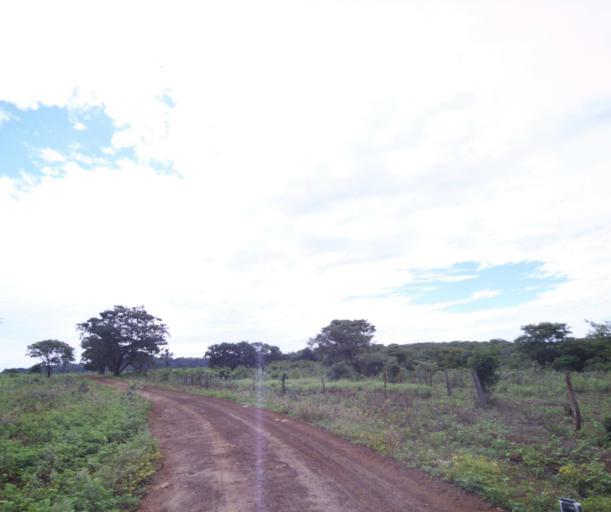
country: BR
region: Bahia
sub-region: Carinhanha
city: Carinhanha
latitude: -14.2467
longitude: -44.4234
